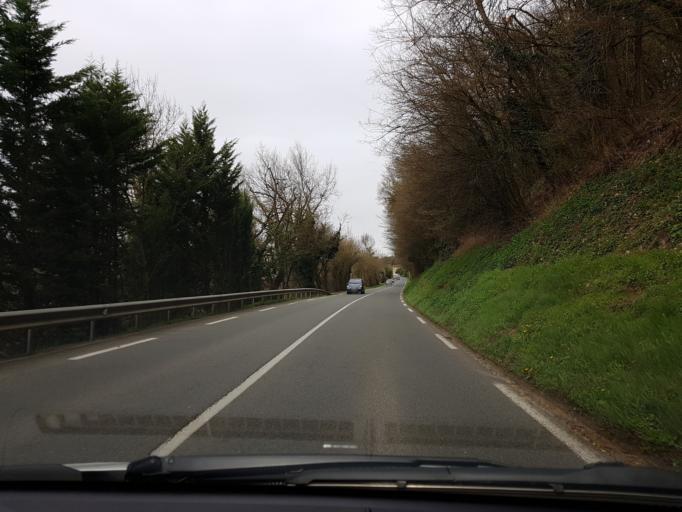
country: FR
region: Rhone-Alpes
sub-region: Departement de l'Ain
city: Jassans-Riottier
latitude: 45.9639
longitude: 4.7526
